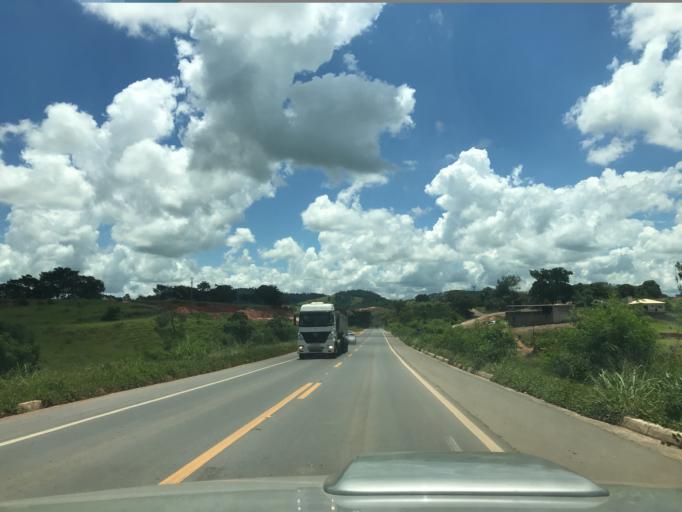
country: BR
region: Minas Gerais
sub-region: Perdoes
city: Perdoes
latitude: -21.1037
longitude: -45.0952
